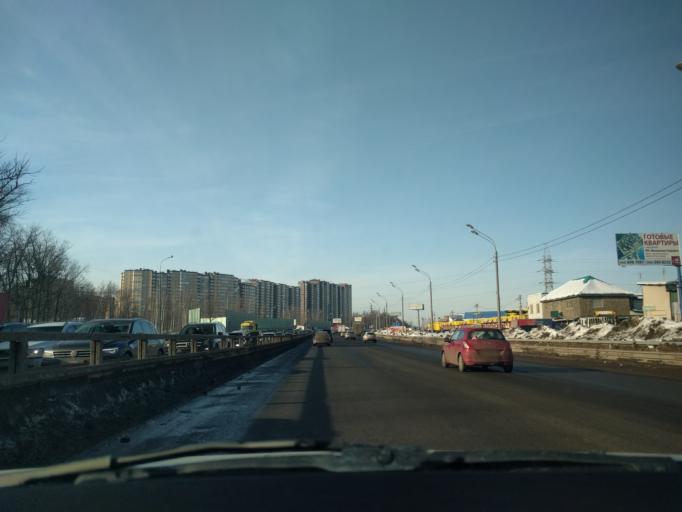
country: RU
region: Moscow
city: Severnyy
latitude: 55.9575
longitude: 37.5343
